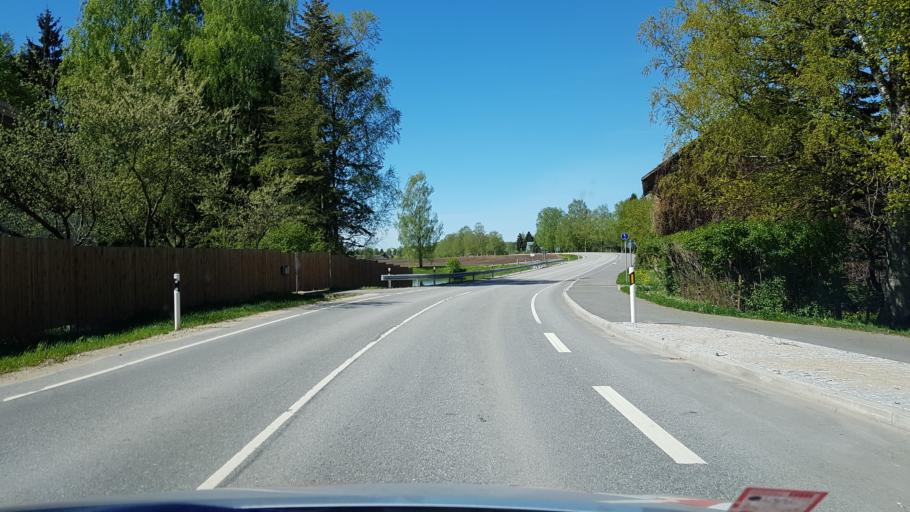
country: EE
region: Tartu
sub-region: Noo vald
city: Noo
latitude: 58.3884
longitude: 26.5811
